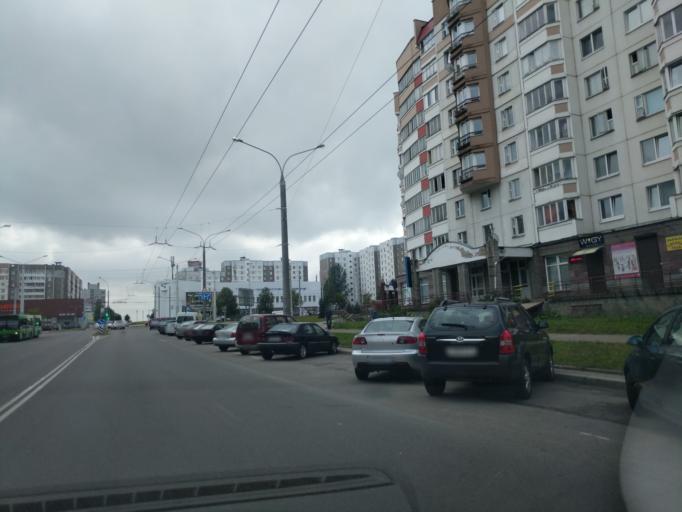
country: BY
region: Minsk
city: Novoye Medvezhino
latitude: 53.8888
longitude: 27.4218
